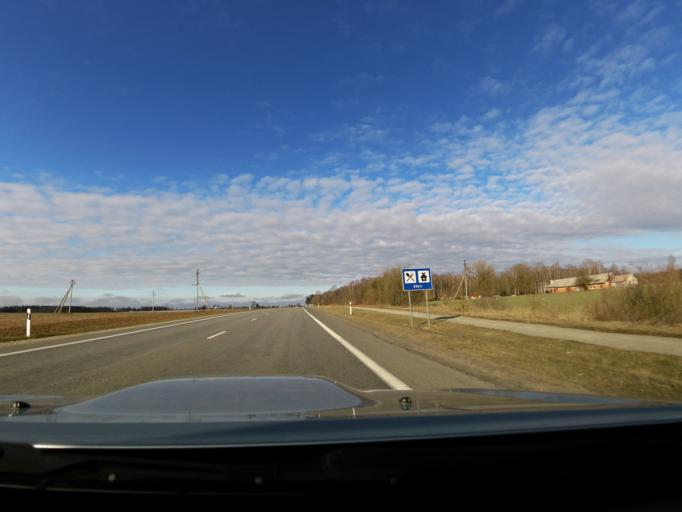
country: LT
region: Panevezys
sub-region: Panevezys City
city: Panevezys
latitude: 55.7343
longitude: 24.2530
